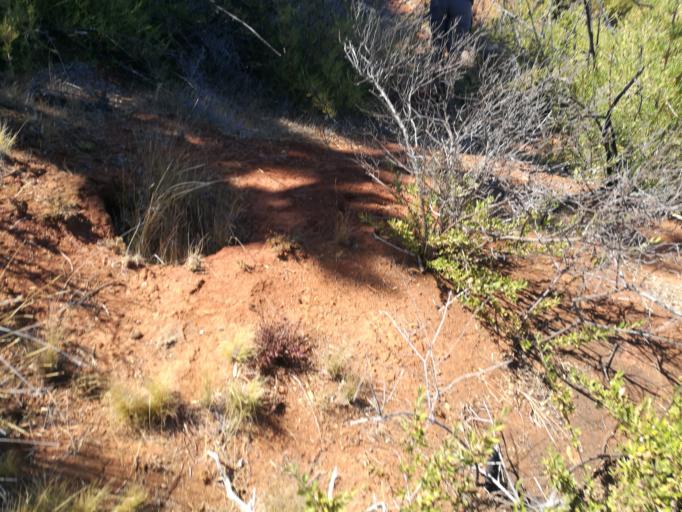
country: CL
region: Valparaiso
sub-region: Provincia de Valparaiso
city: Valparaiso
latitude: -33.0718
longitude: -71.6536
